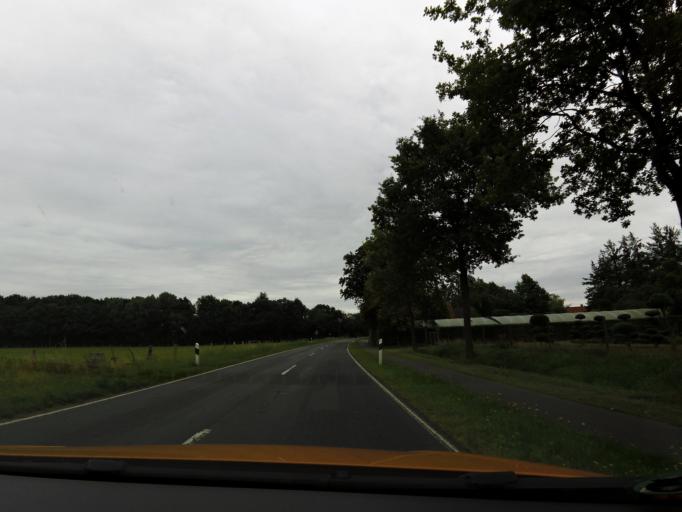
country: DE
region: Lower Saxony
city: Wiefelstede
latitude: 53.2110
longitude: 8.0848
